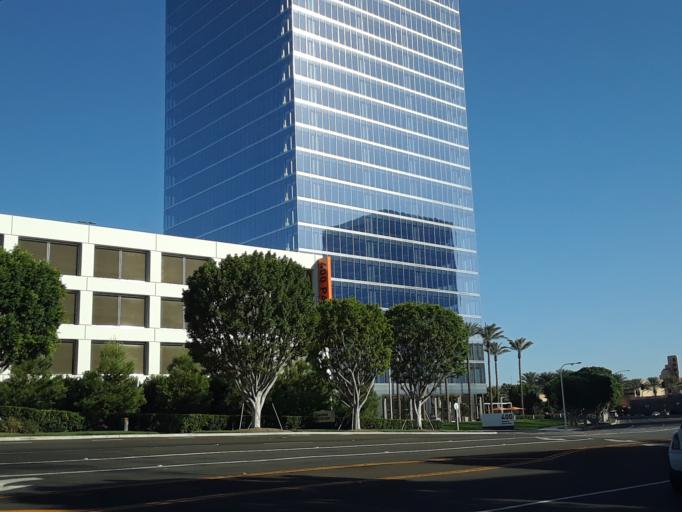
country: US
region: California
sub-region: Orange County
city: Laguna Woods
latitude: 33.6552
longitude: -117.7470
